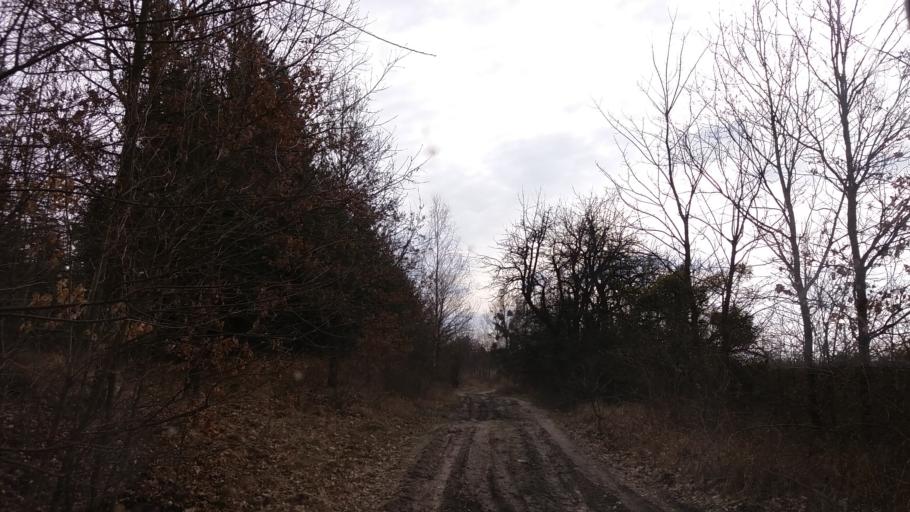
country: PL
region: West Pomeranian Voivodeship
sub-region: Powiat choszczenski
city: Bierzwnik
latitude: 53.1243
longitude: 15.6296
